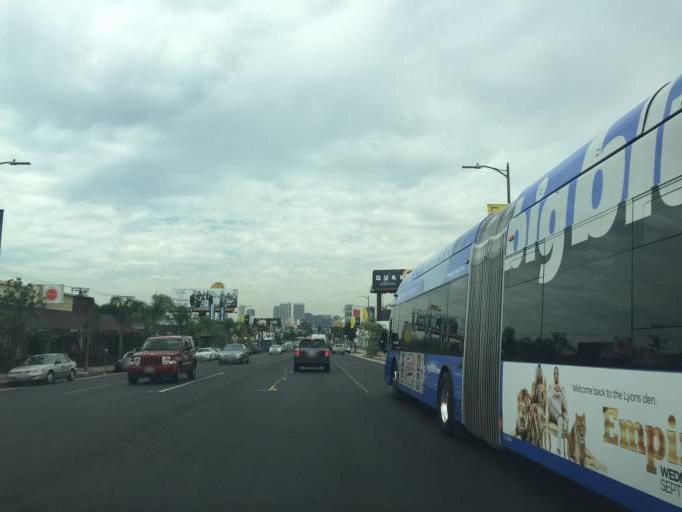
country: US
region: California
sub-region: Los Angeles County
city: Beverly Hills
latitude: 34.0530
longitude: -118.3738
